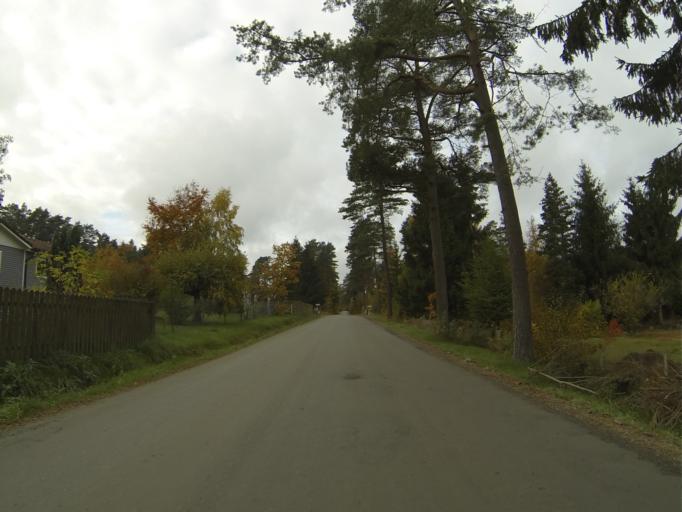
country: SE
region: Skane
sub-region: Sjobo Kommun
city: Sjoebo
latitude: 55.6335
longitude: 13.6500
